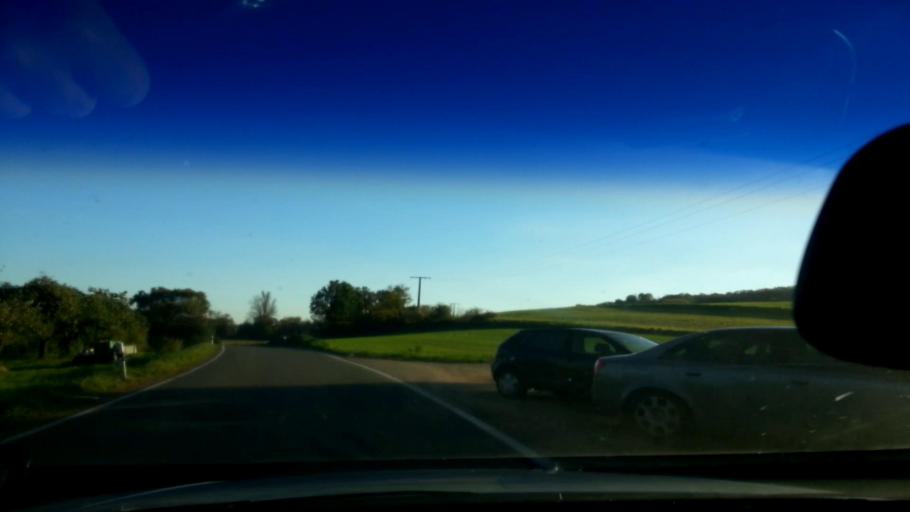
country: DE
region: Bavaria
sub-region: Upper Franconia
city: Rattelsdorf
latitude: 50.0124
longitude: 10.8727
